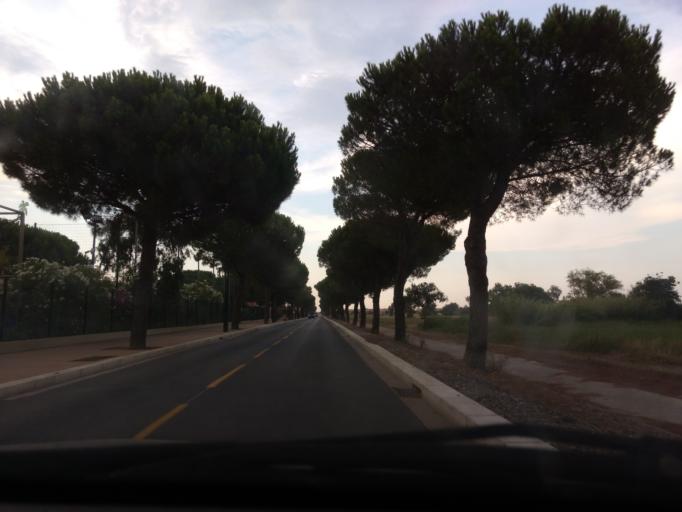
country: FR
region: Languedoc-Roussillon
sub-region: Departement des Pyrenees-Orientales
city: Le Barcares
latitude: 42.7791
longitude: 3.0307
